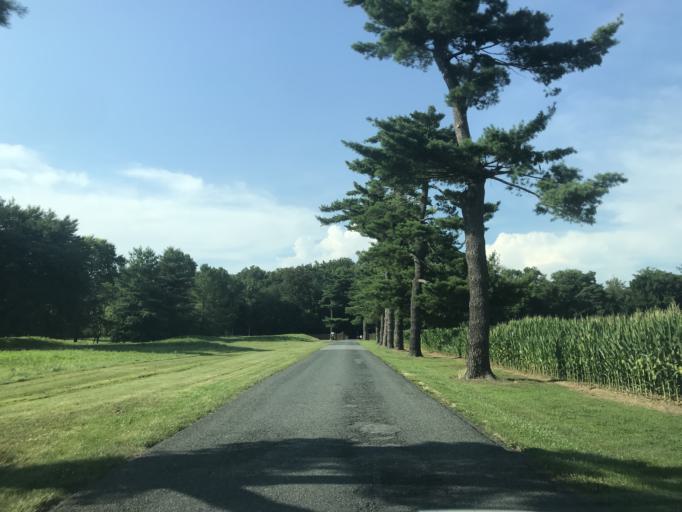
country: US
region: Maryland
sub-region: Harford County
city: Aberdeen
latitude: 39.5109
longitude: -76.1258
